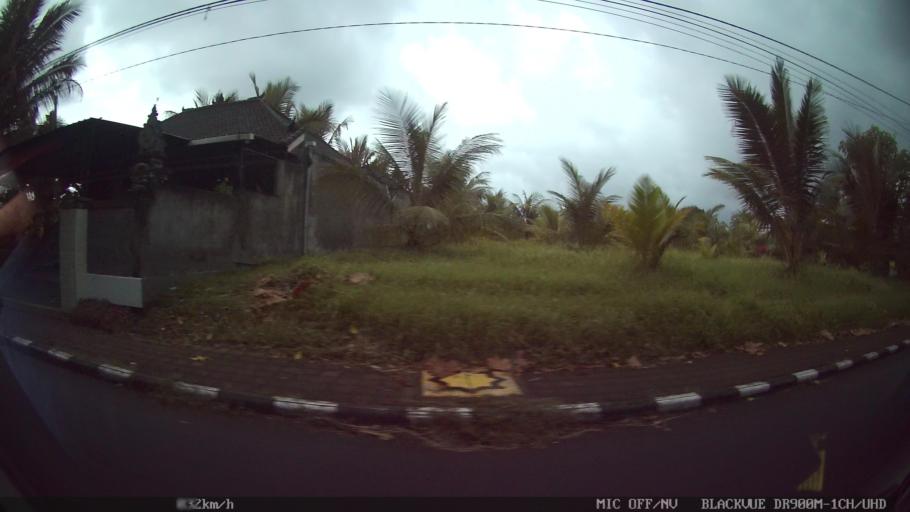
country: ID
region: Bali
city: Banjar Sempidi
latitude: -8.5172
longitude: 115.2051
